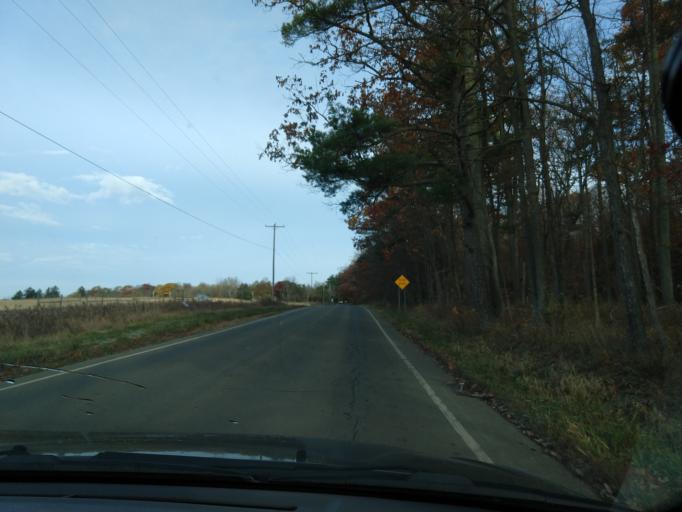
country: US
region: New York
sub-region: Tompkins County
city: Northeast Ithaca
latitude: 42.4654
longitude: -76.4463
